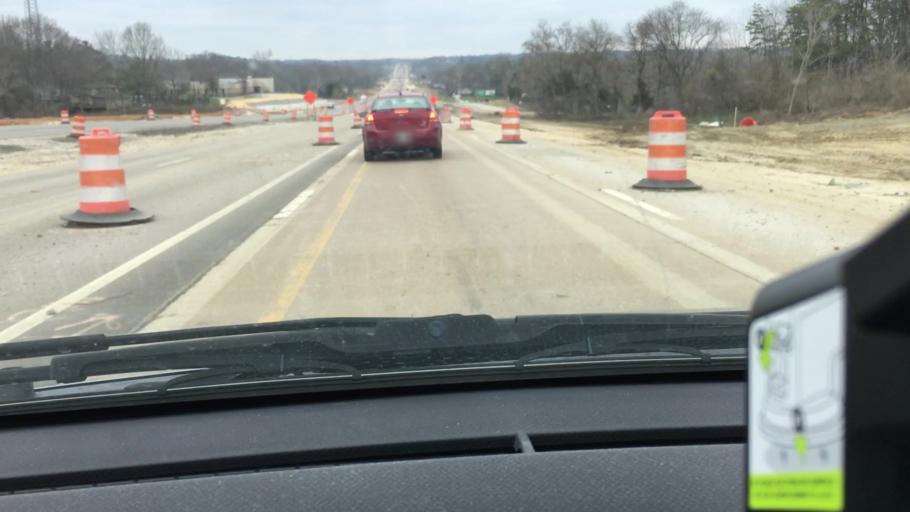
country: US
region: Indiana
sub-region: Monroe County
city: Bloomington
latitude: 39.2491
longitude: -86.5312
